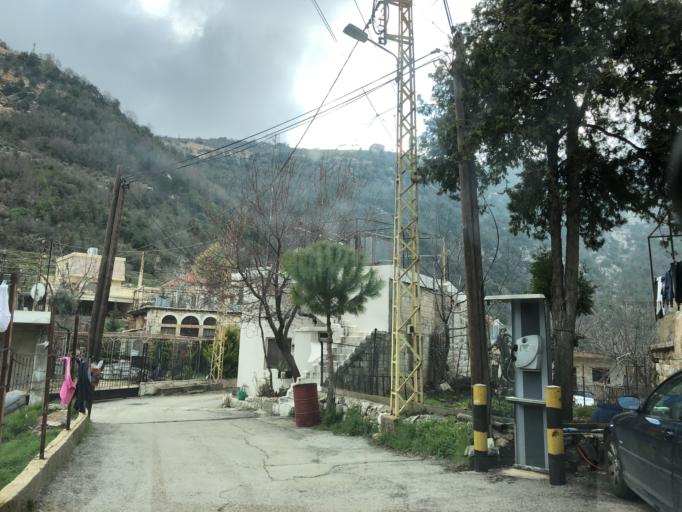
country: LB
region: Liban-Nord
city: Amioun
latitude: 34.2065
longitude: 35.8362
